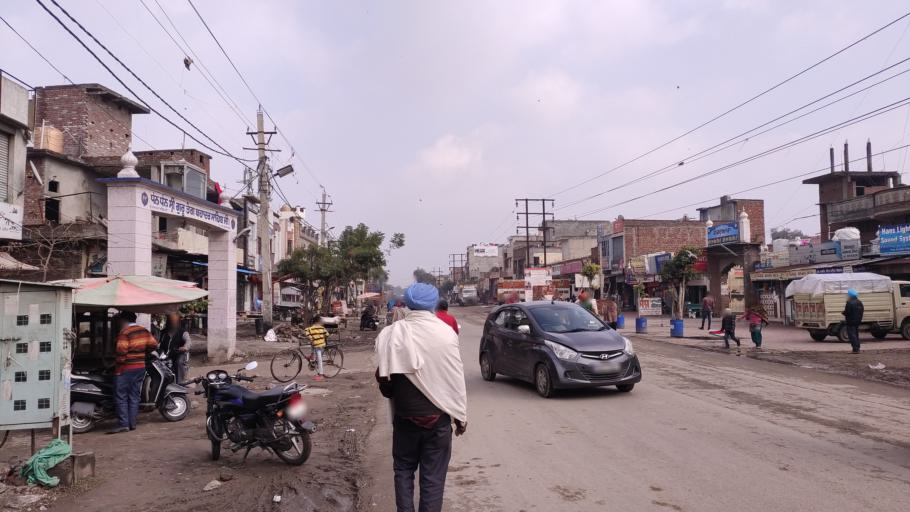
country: IN
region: Punjab
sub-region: Amritsar
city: Amritsar
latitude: 31.6228
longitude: 74.9073
